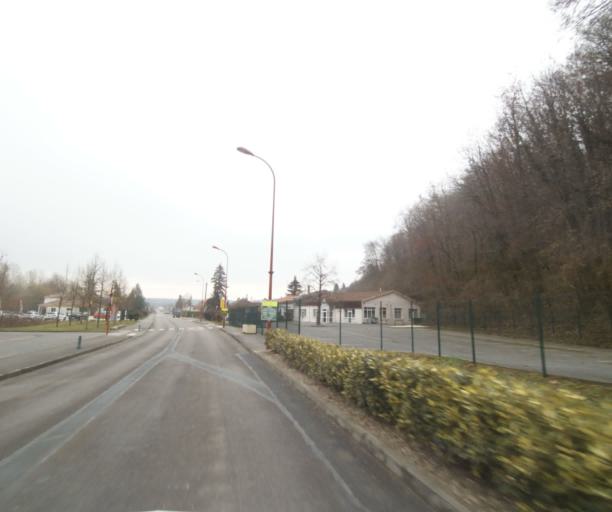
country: FR
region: Champagne-Ardenne
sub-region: Departement de la Haute-Marne
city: Bienville
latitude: 48.5465
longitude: 5.0780
